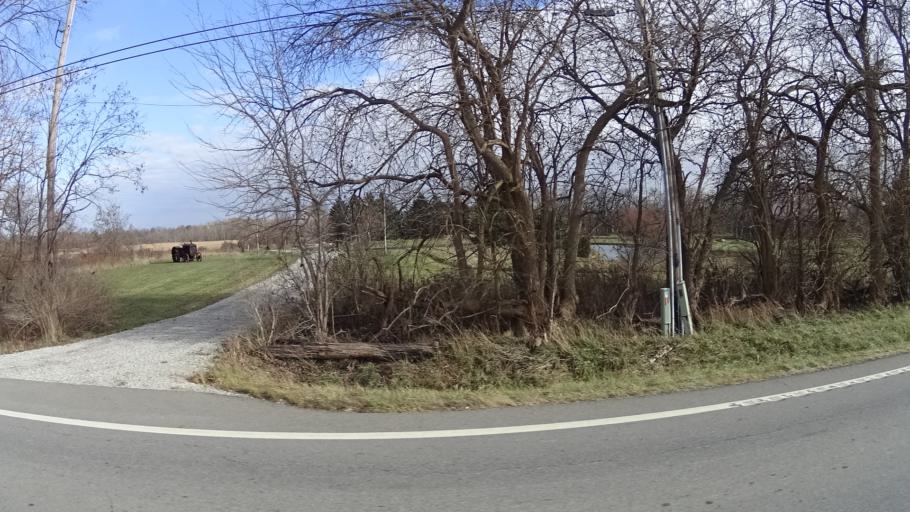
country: US
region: Ohio
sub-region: Lorain County
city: Camden
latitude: 41.1604
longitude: -82.3098
